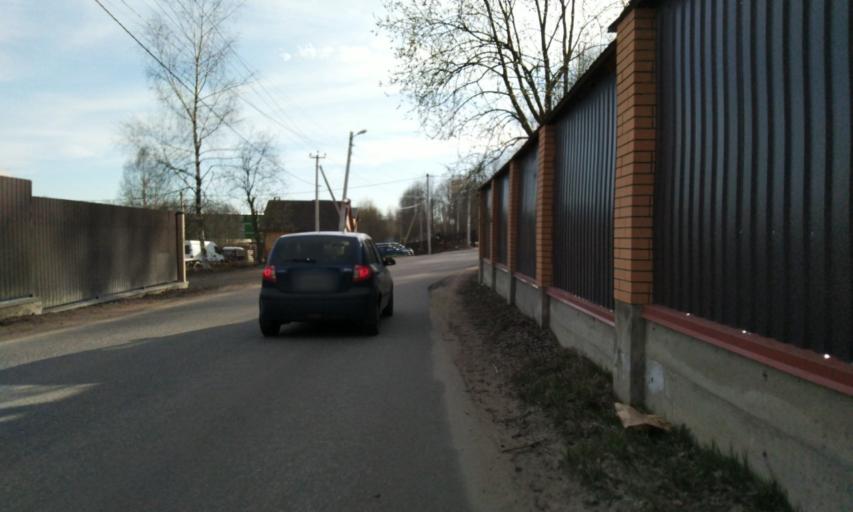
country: RU
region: Leningrad
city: Bugry
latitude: 60.1129
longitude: 30.4260
